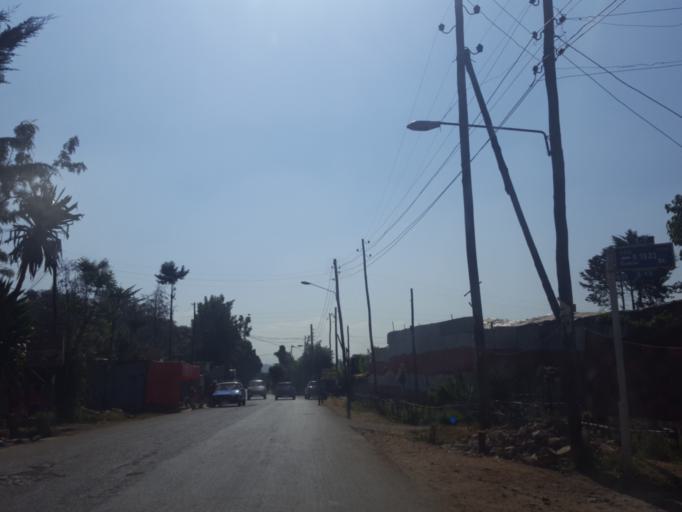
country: ET
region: Adis Abeba
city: Addis Ababa
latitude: 9.0509
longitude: 38.7337
